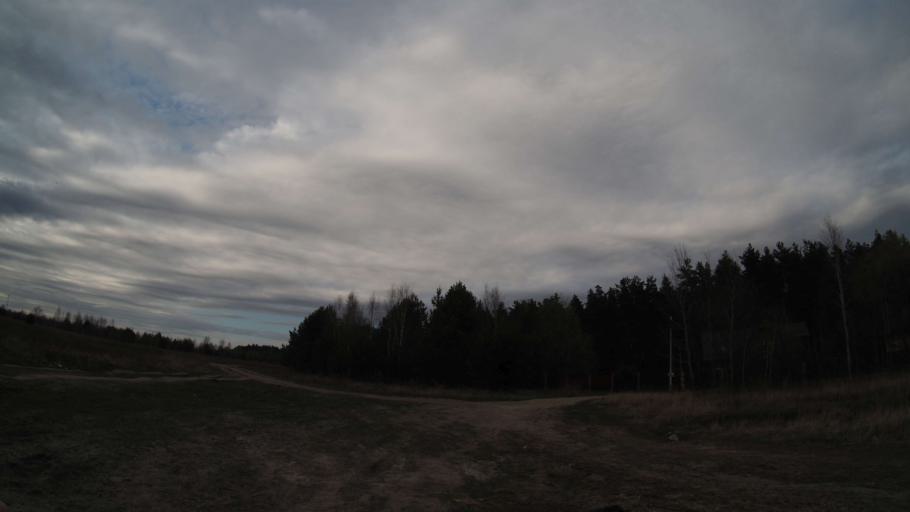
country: RU
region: Moskovskaya
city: Ramenskoye
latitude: 55.5902
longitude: 38.2898
